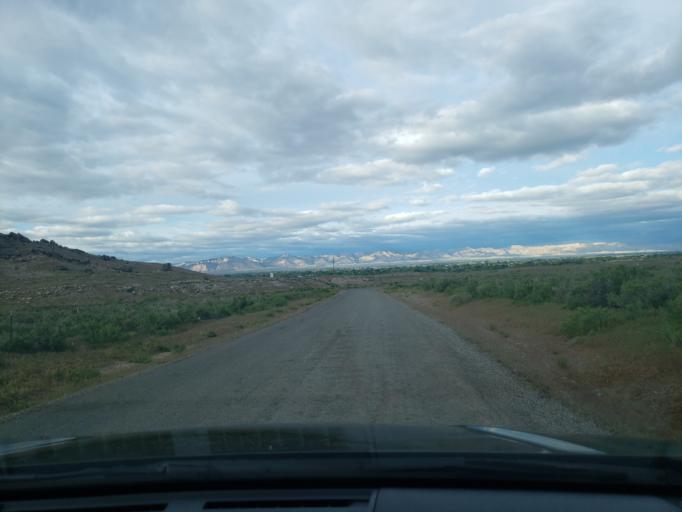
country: US
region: Colorado
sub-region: Mesa County
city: Fruita
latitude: 39.1401
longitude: -108.7561
